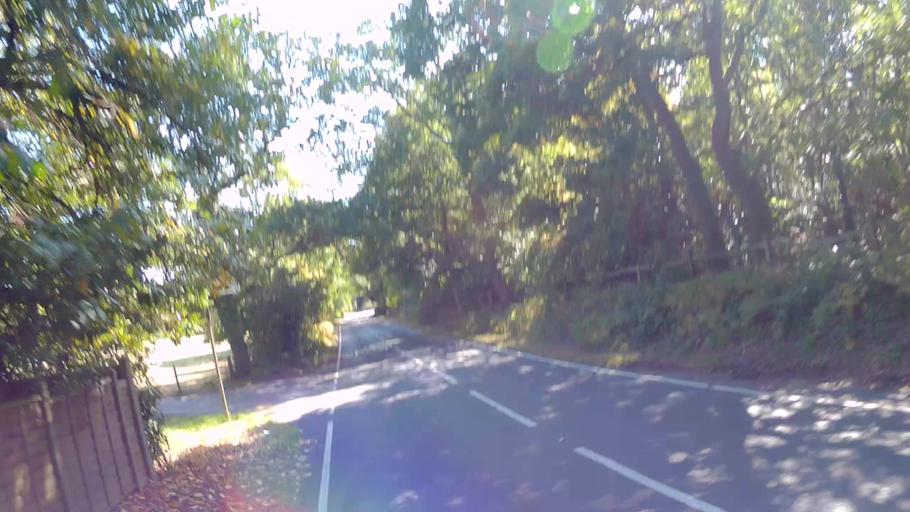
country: GB
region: England
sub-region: Surrey
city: Farnham
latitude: 51.1993
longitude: -0.7737
